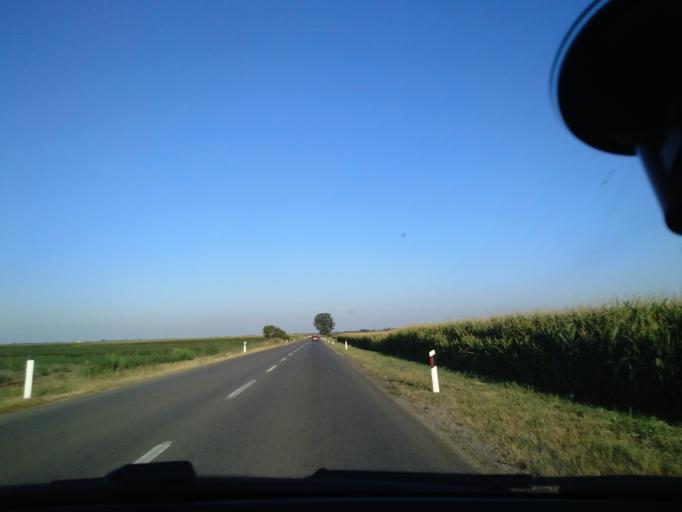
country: RS
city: Maglic
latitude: 45.3872
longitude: 19.4974
